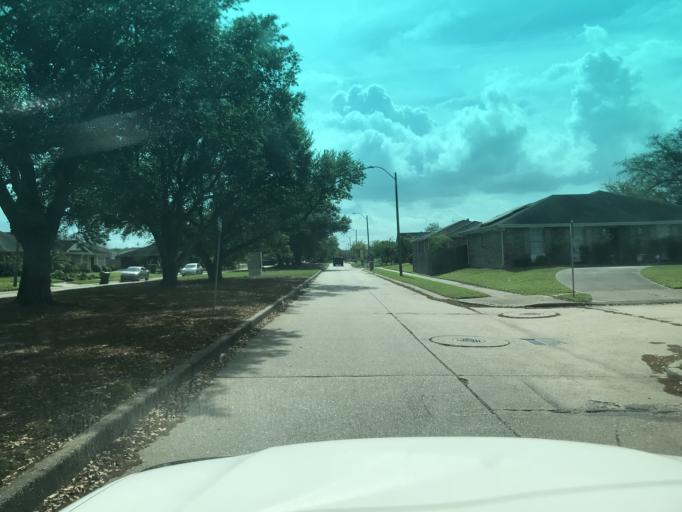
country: US
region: Louisiana
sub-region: Saint Bernard Parish
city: Chalmette
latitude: 30.0376
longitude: -89.9571
